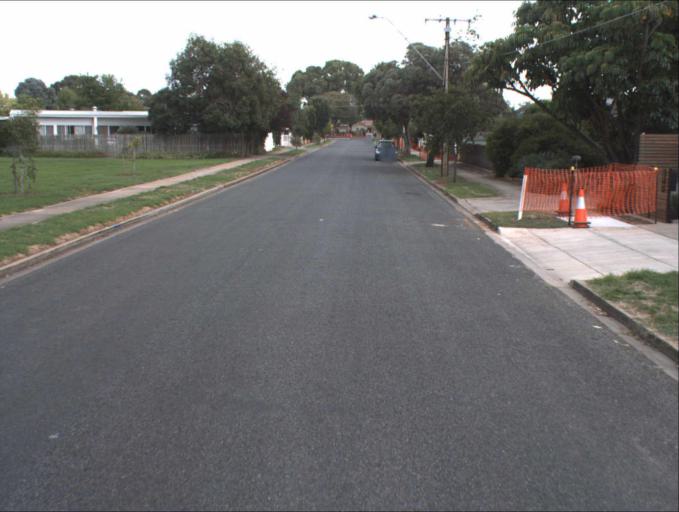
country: AU
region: South Australia
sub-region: Port Adelaide Enfield
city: Klemzig
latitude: -34.8796
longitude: 138.6395
